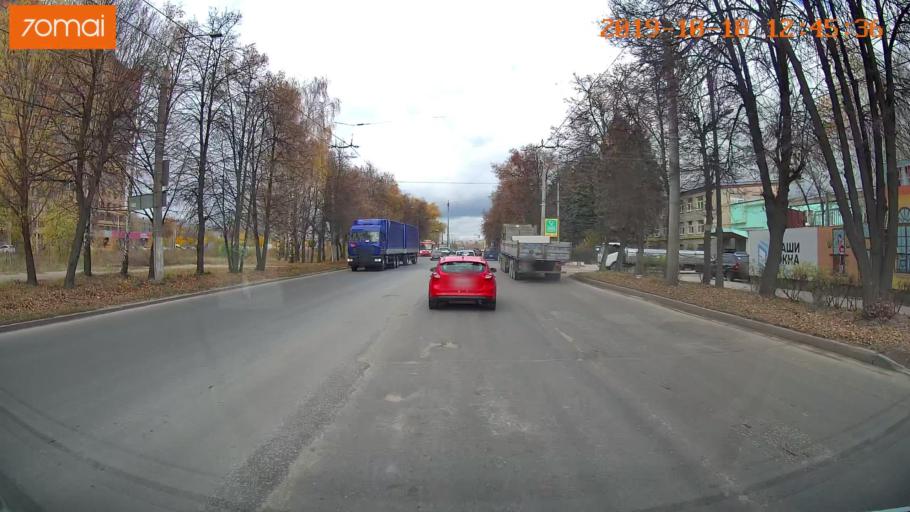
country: RU
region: Rjazan
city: Ryazan'
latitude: 54.6529
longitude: 39.6660
